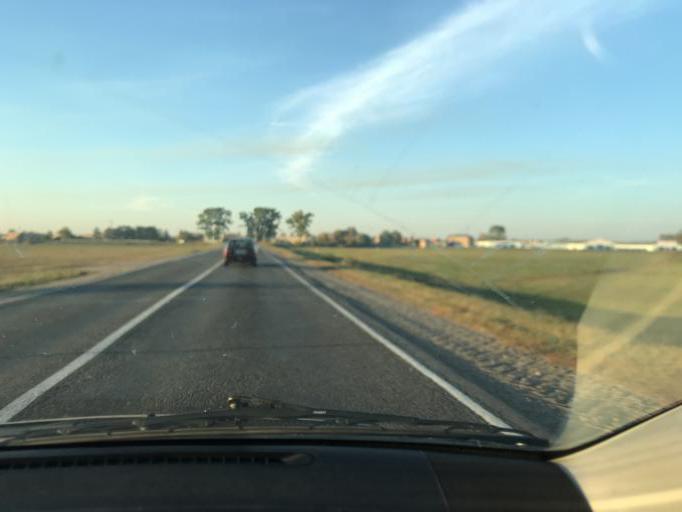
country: BY
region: Brest
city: Pinsk
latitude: 52.0608
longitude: 26.2103
